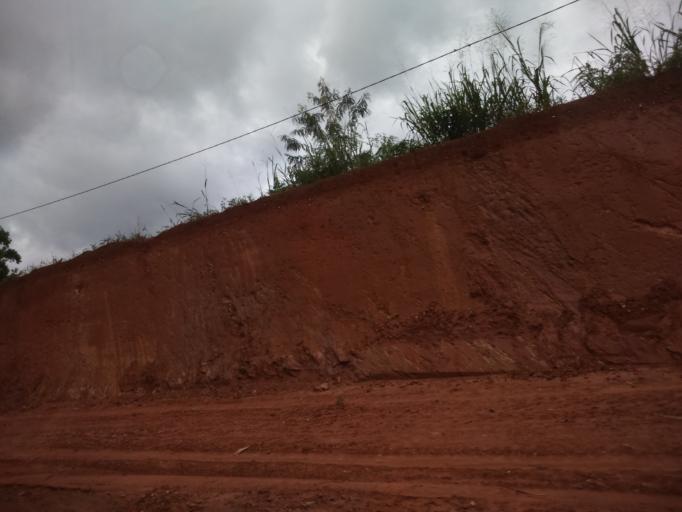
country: CI
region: Moyen-Comoe
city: Abengourou
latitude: 6.6270
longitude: -3.7109
